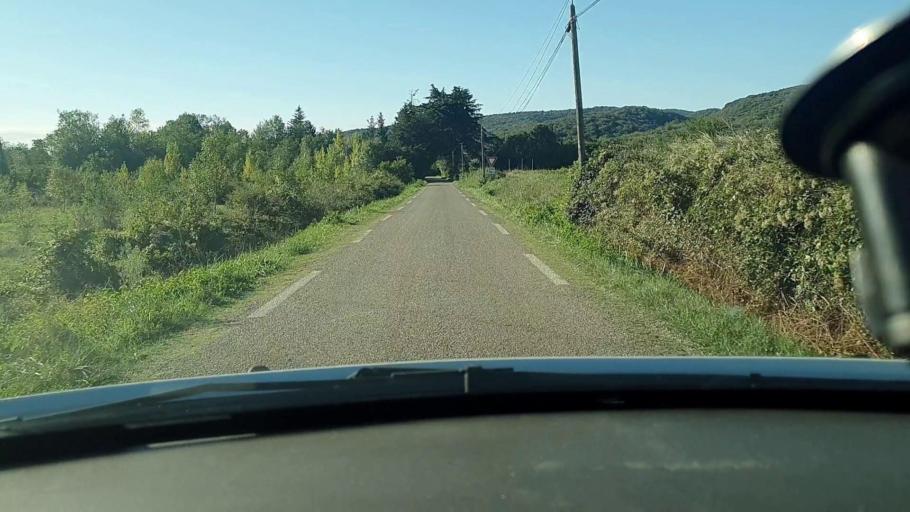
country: FR
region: Languedoc-Roussillon
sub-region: Departement du Gard
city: Goudargues
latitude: 44.2377
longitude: 4.4421
